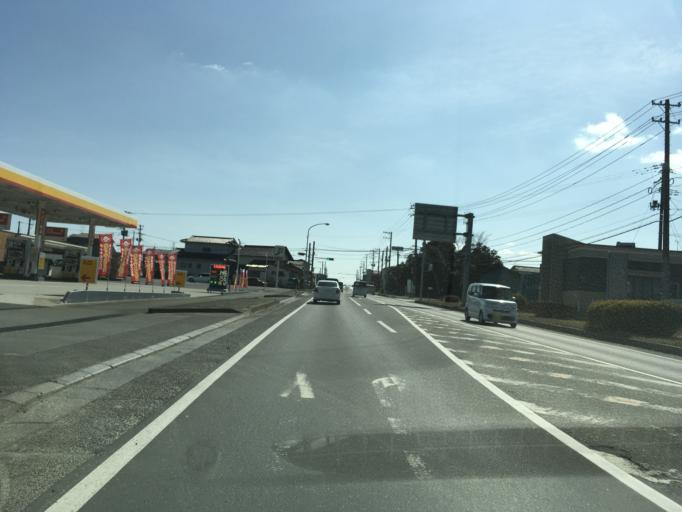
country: JP
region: Iwate
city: Ofunato
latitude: 38.8643
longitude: 141.5797
